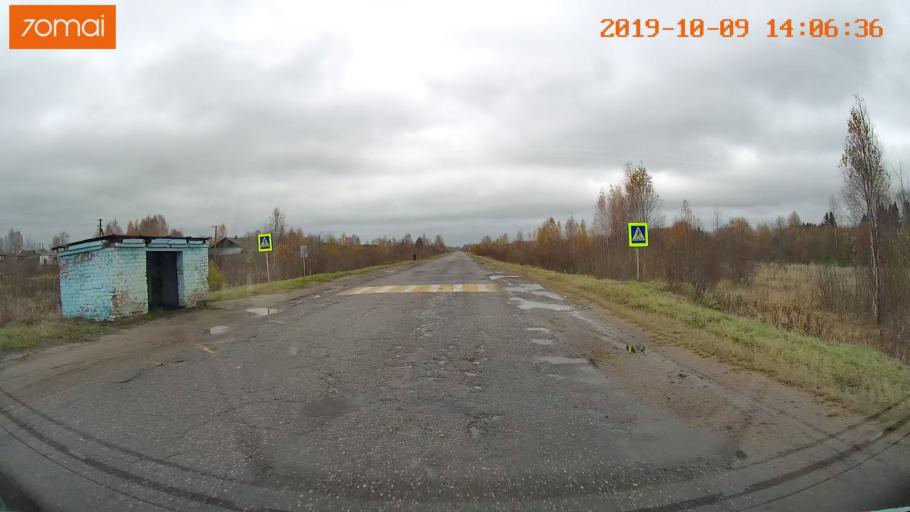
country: RU
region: Kostroma
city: Buy
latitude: 58.4656
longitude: 41.4125
